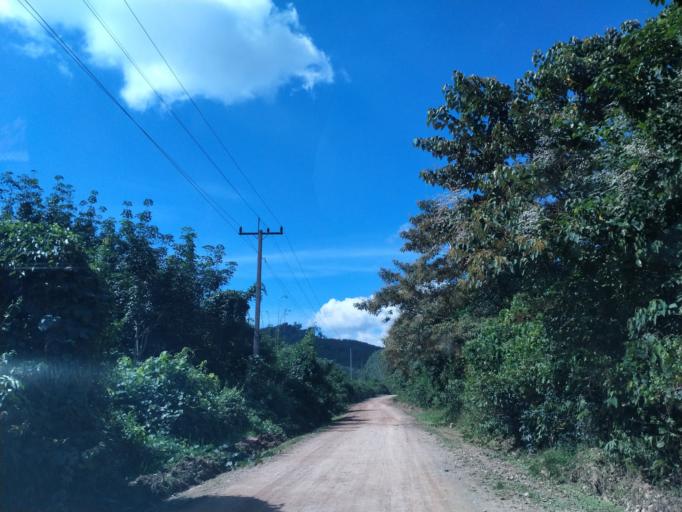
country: TH
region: Changwat Bueng Kan
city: Pak Khat
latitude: 18.6390
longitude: 103.0048
